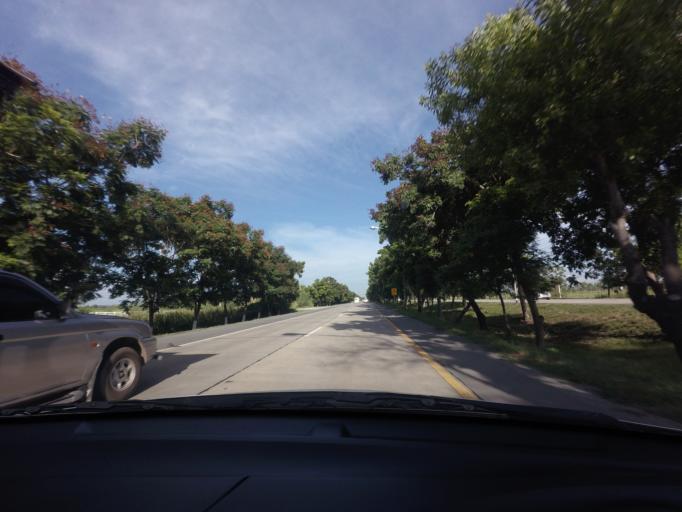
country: TH
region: Suphan Buri
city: Bang Pla Ma
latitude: 14.3377
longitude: 100.1987
